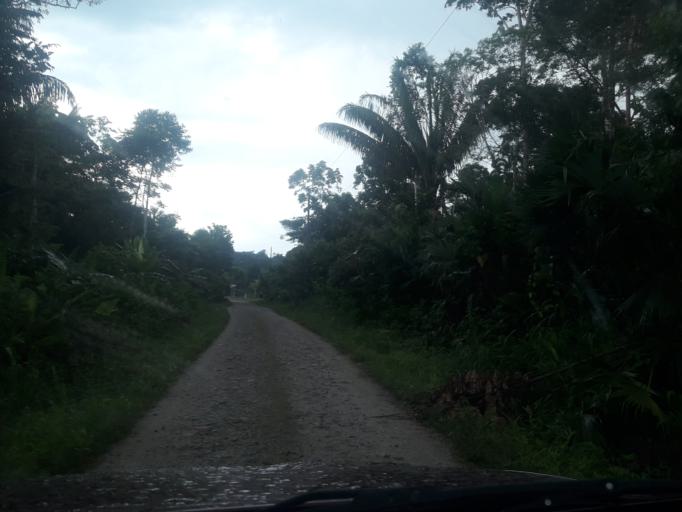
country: EC
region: Napo
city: Tena
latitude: -1.0979
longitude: -77.6821
